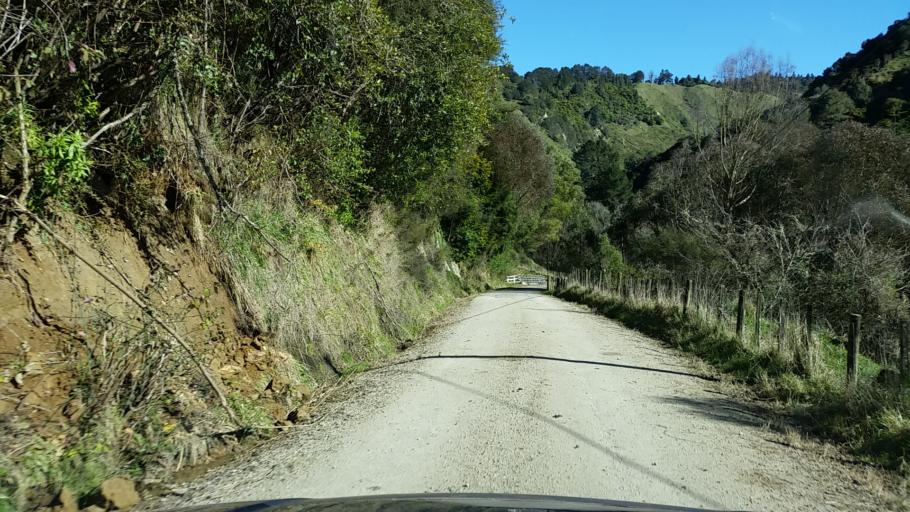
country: NZ
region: Manawatu-Wanganui
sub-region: Wanganui District
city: Wanganui
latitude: -39.5431
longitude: 174.9059
